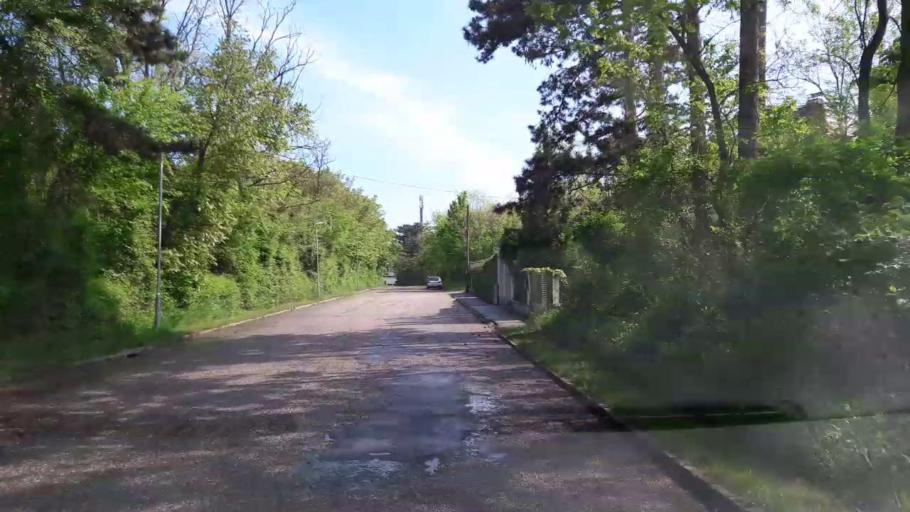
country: AT
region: Lower Austria
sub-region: Politischer Bezirk Ganserndorf
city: Deutsch-Wagram
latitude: 48.3088
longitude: 16.5778
